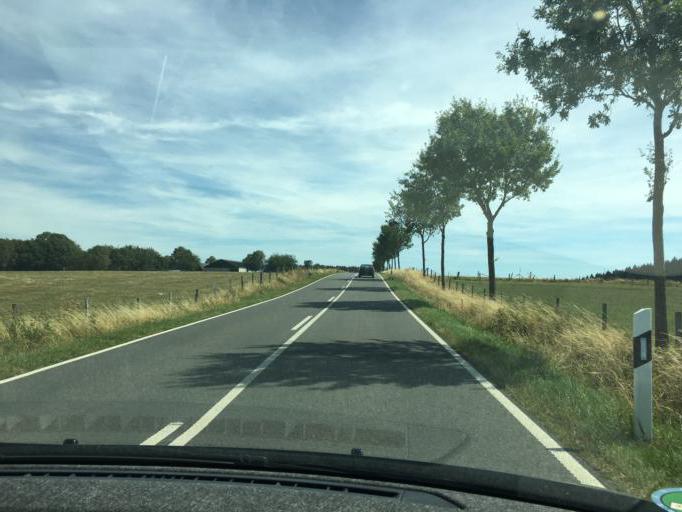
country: DE
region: North Rhine-Westphalia
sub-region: Regierungsbezirk Koln
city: Hurtgenwald
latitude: 50.6689
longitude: 6.3282
